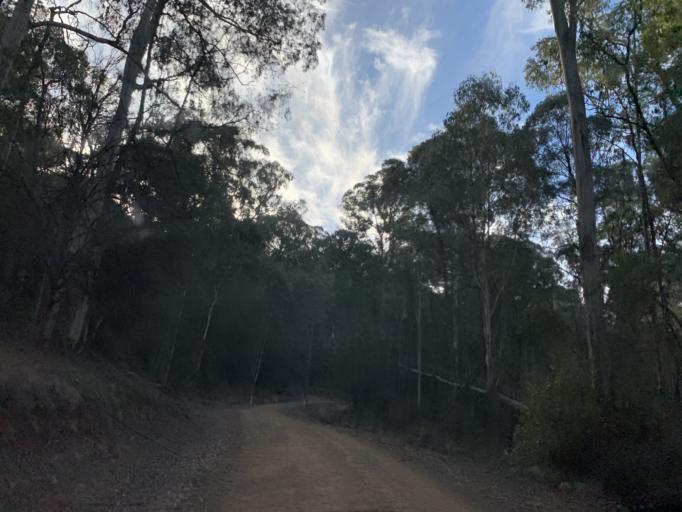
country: AU
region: Victoria
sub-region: Mansfield
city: Mansfield
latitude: -36.8879
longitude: 146.1212
